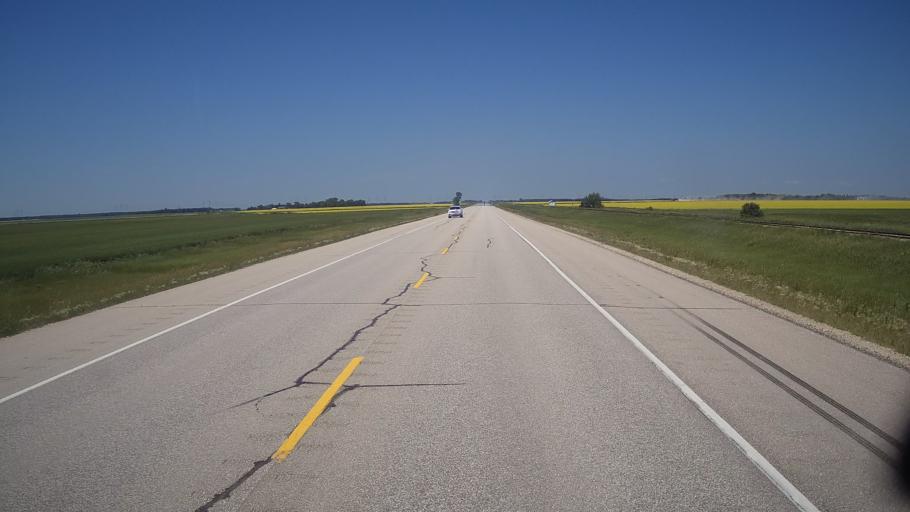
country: CA
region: Manitoba
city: Stonewall
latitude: 50.0249
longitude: -97.3821
